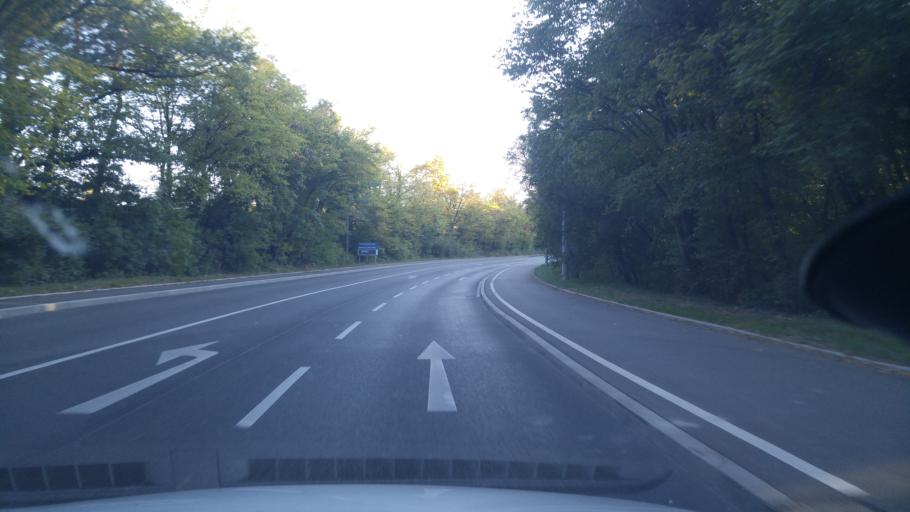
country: DE
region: Baden-Wuerttemberg
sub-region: Regierungsbezirk Stuttgart
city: Stuttgart Feuerbach
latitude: 48.7898
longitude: 9.1518
